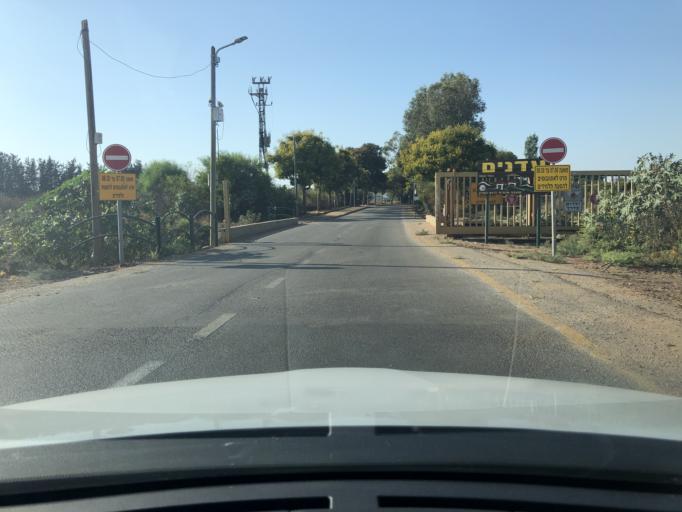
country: IL
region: Central District
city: Hod HaSharon
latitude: 32.1345
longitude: 34.9089
